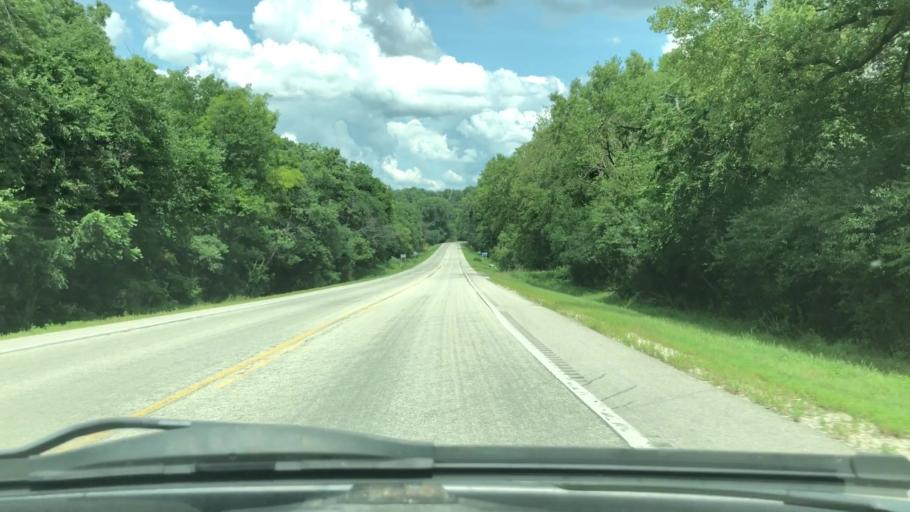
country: US
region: Minnesota
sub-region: Olmsted County
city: Rochester
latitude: 43.9713
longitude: -92.5180
